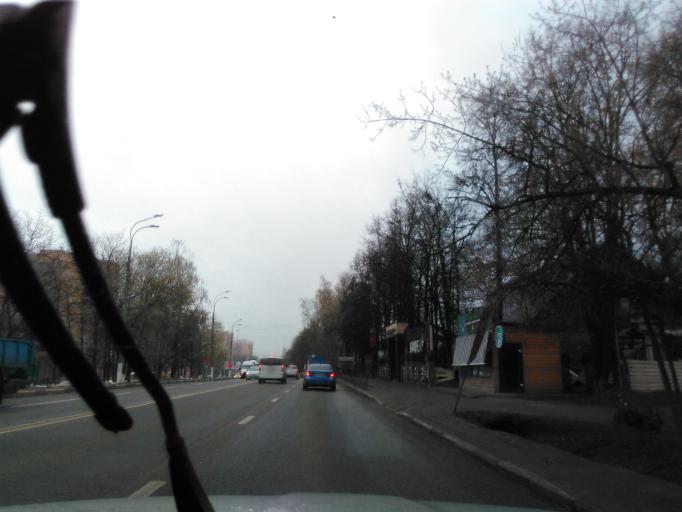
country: RU
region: Moskovskaya
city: Krasnogorsk
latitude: 55.8288
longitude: 37.3077
